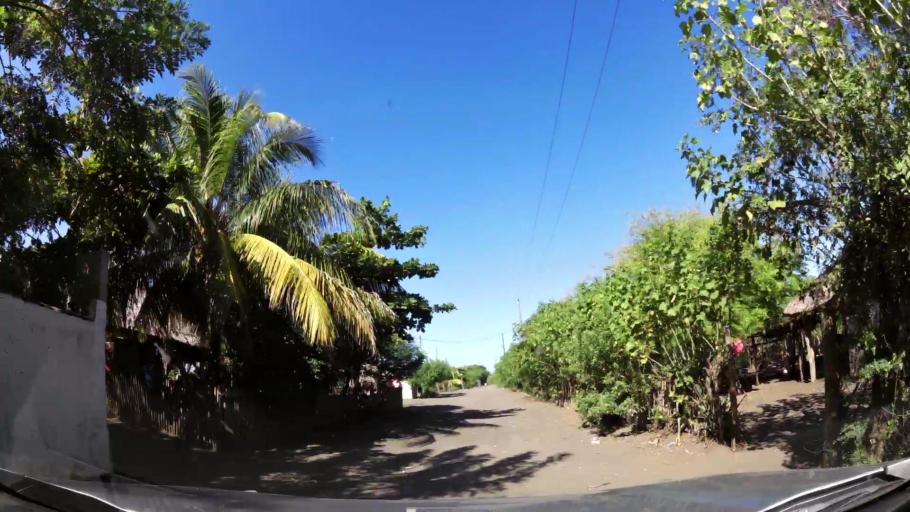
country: GT
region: Jutiapa
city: Pasaco
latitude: 13.8454
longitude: -90.3623
